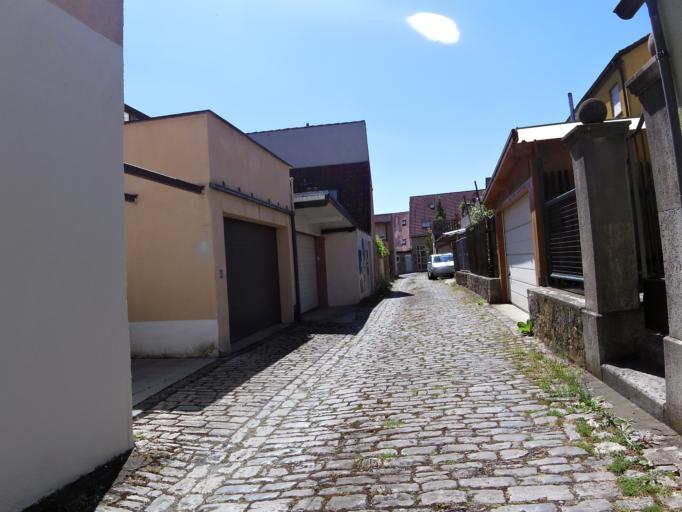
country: DE
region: Bavaria
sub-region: Regierungsbezirk Unterfranken
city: Randersacker
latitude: 49.7612
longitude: 9.9871
